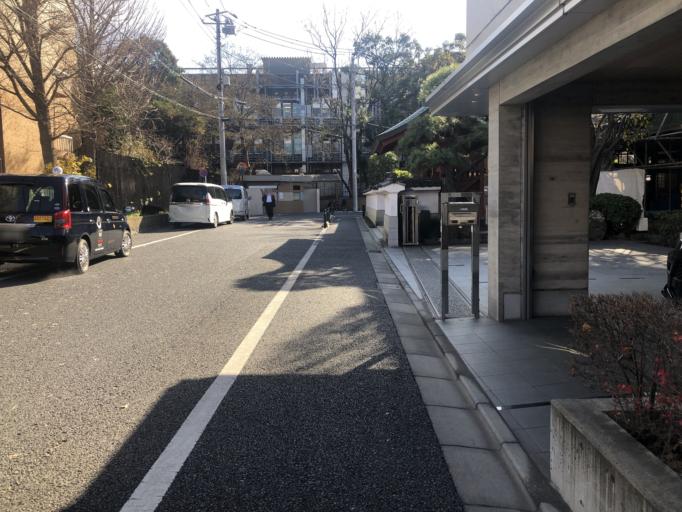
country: JP
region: Tokyo
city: Tokyo
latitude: 35.7175
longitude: 139.7591
